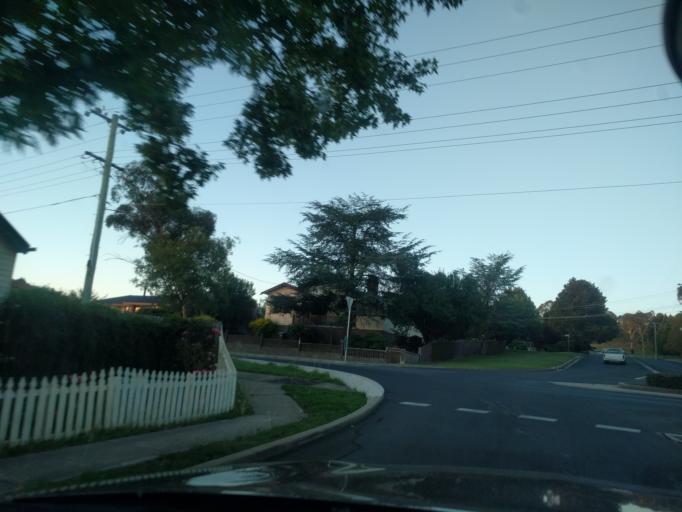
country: AU
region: New South Wales
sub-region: Armidale Dumaresq
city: Armidale
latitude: -30.5062
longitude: 151.6611
